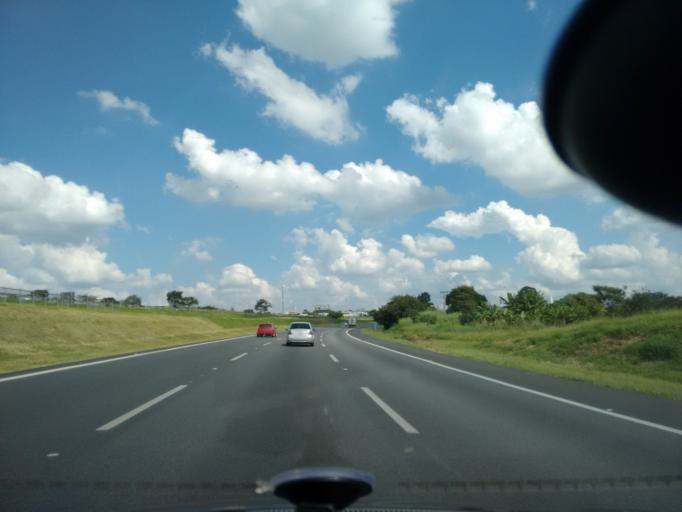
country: BR
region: Sao Paulo
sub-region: Campinas
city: Campinas
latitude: -22.9781
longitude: -47.1125
